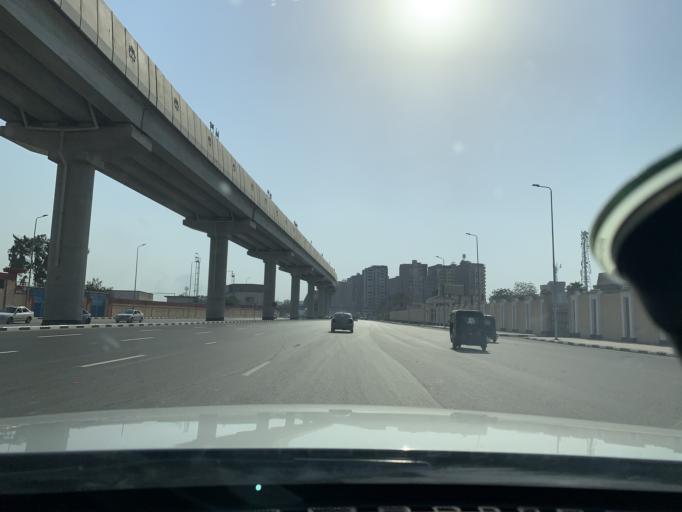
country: EG
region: Muhafazat al Qalyubiyah
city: Al Khankah
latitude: 30.1289
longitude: 31.3659
